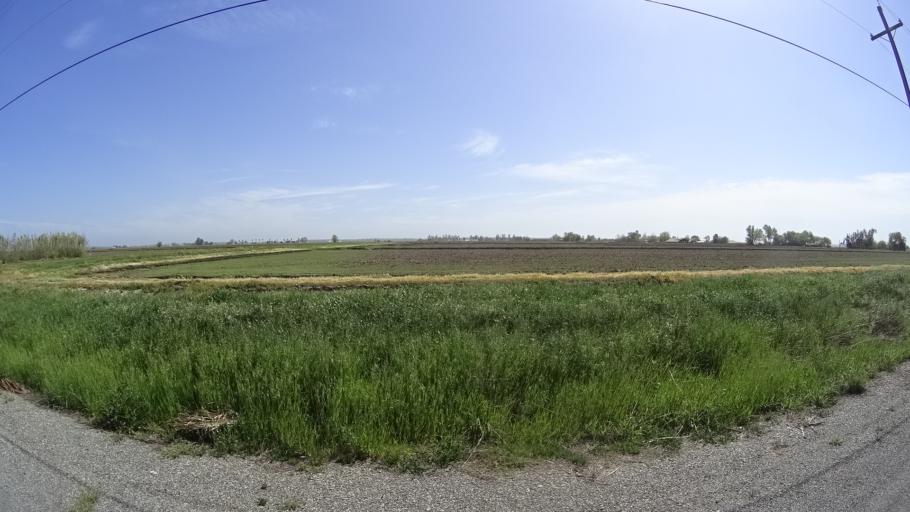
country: US
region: California
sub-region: Glenn County
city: Willows
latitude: 39.5866
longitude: -122.0557
